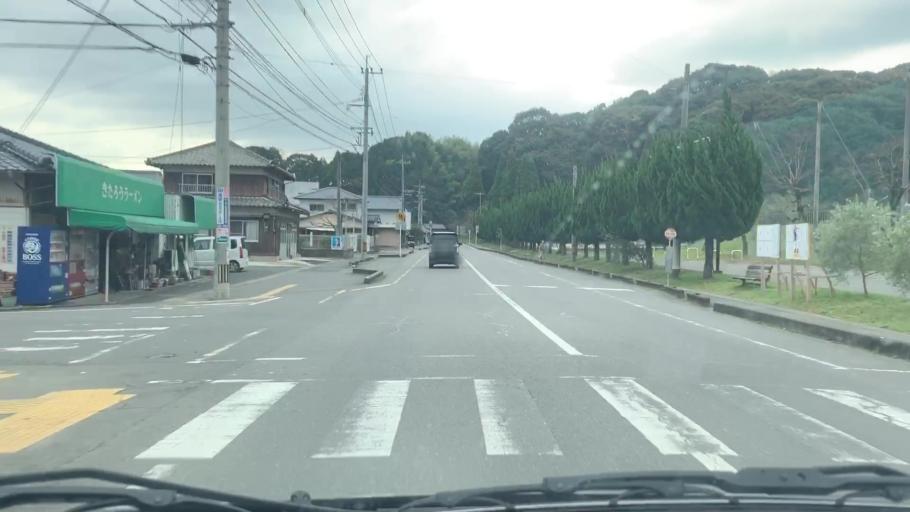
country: JP
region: Saga Prefecture
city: Takeocho-takeo
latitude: 33.1931
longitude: 130.0310
